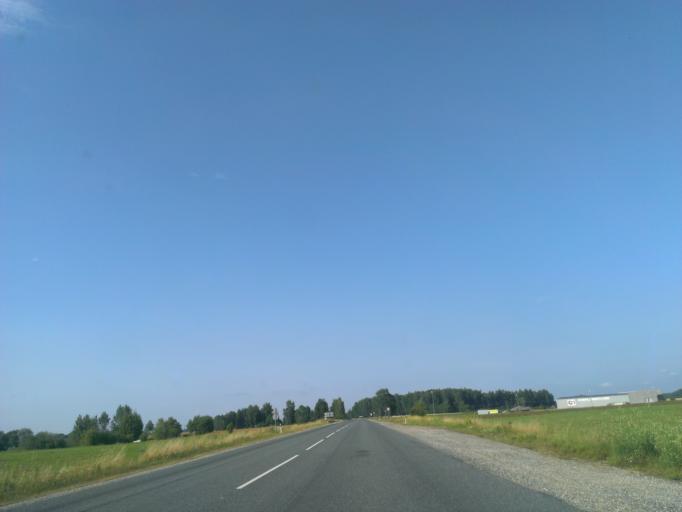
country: LV
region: Priekuli
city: Priekuli
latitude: 57.3135
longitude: 25.3192
